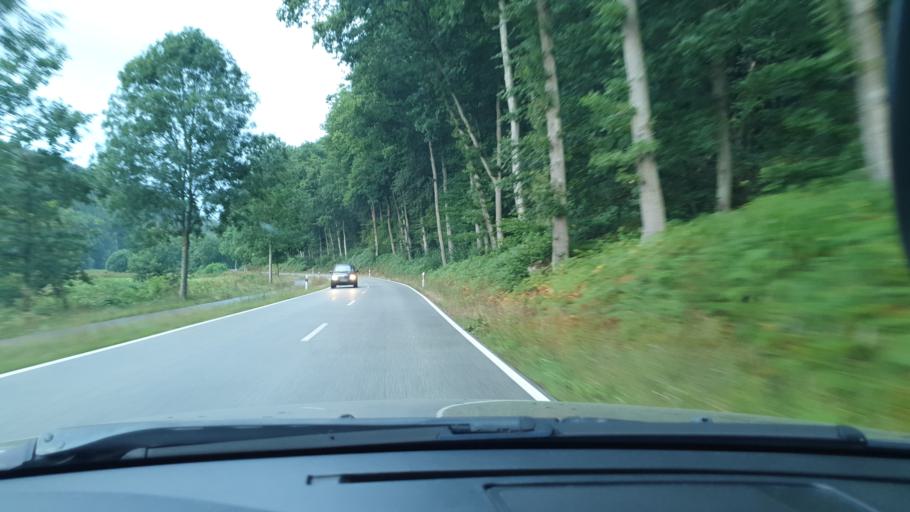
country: DE
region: Rheinland-Pfalz
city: Hettenhausen
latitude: 49.3347
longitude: 7.5505
